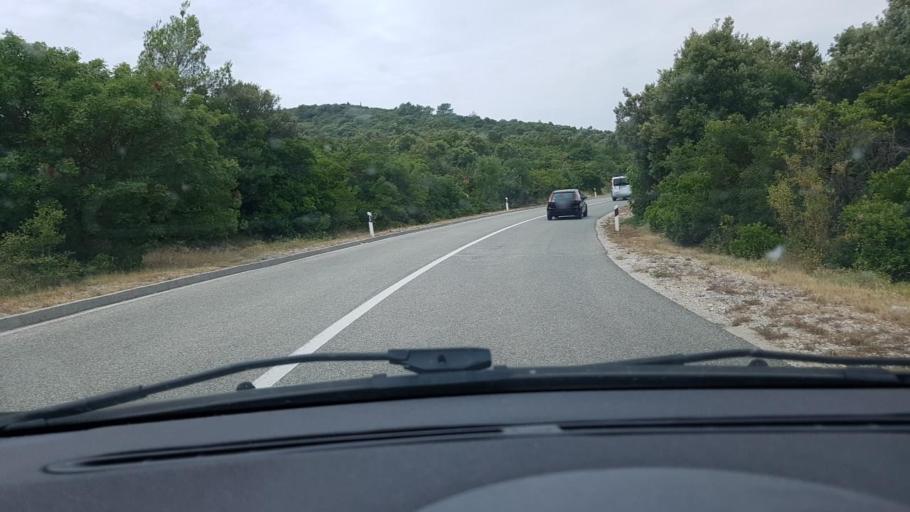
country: HR
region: Dubrovacko-Neretvanska
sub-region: Grad Korcula
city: Zrnovo
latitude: 42.9409
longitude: 17.0561
